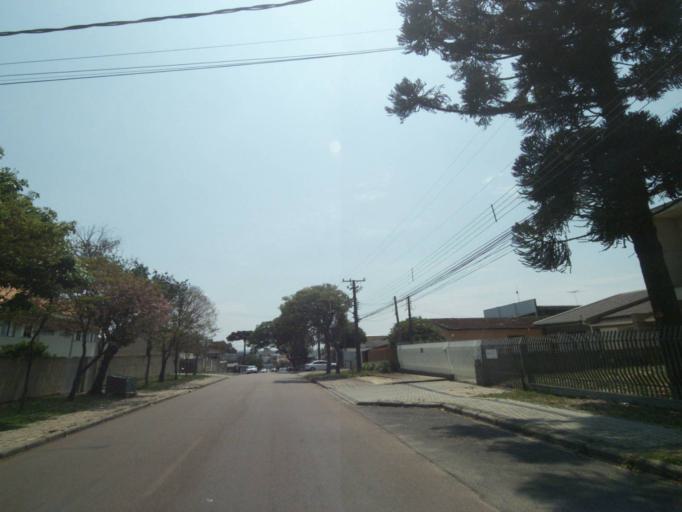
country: BR
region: Parana
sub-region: Curitiba
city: Curitiba
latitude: -25.4792
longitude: -49.3096
